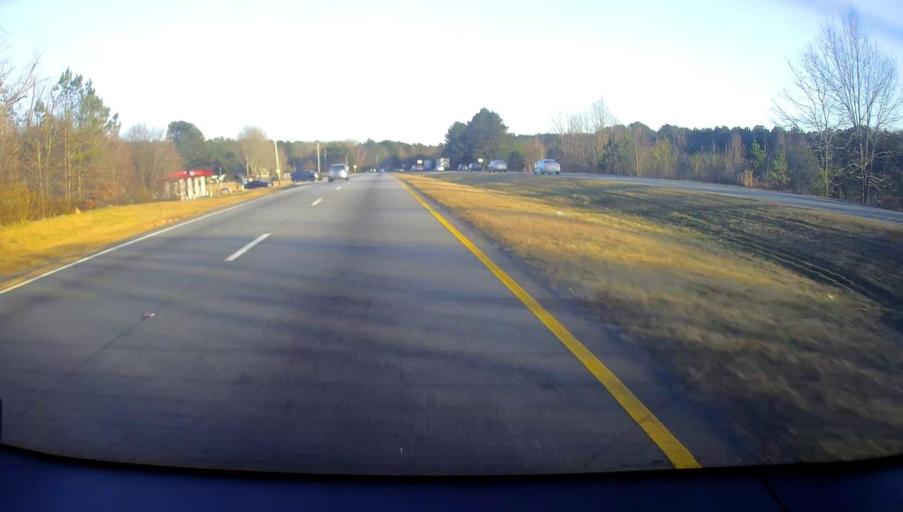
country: US
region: Georgia
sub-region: Fulton County
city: Fairburn
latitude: 33.5531
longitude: -84.5834
